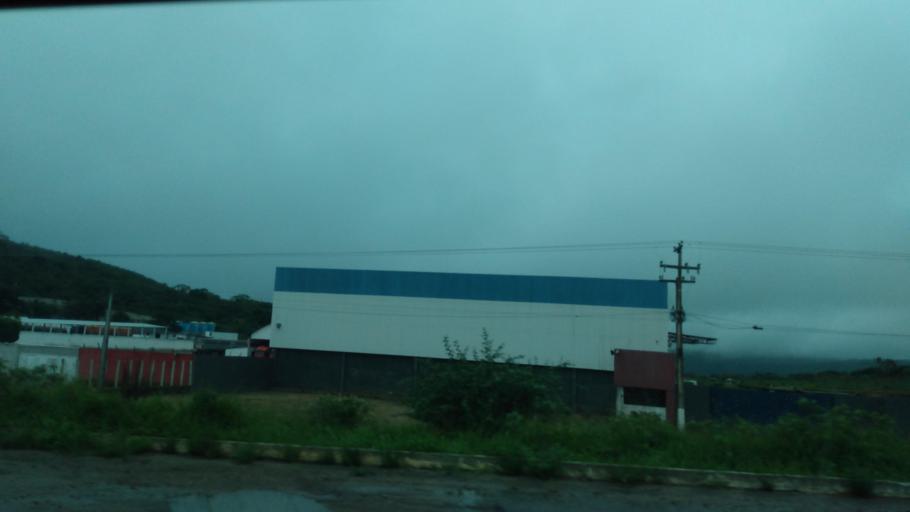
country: BR
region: Pernambuco
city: Garanhuns
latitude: -8.8745
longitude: -36.5250
